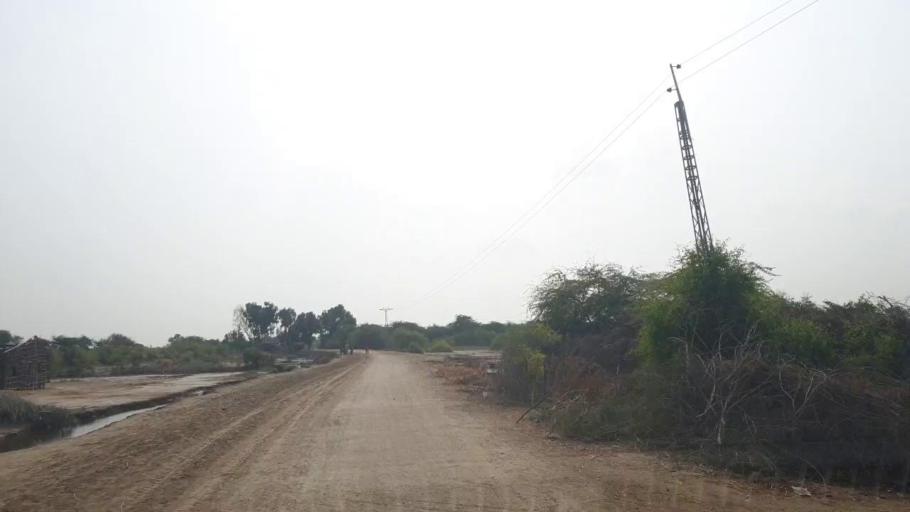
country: PK
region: Sindh
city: Badin
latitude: 24.5436
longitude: 68.6548
